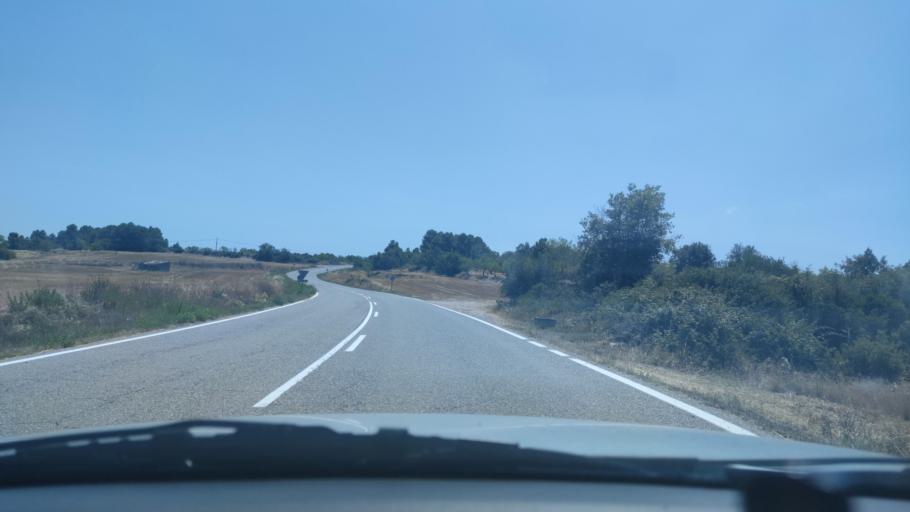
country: ES
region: Catalonia
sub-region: Provincia de Lleida
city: Vinaixa
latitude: 41.4222
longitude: 0.9504
